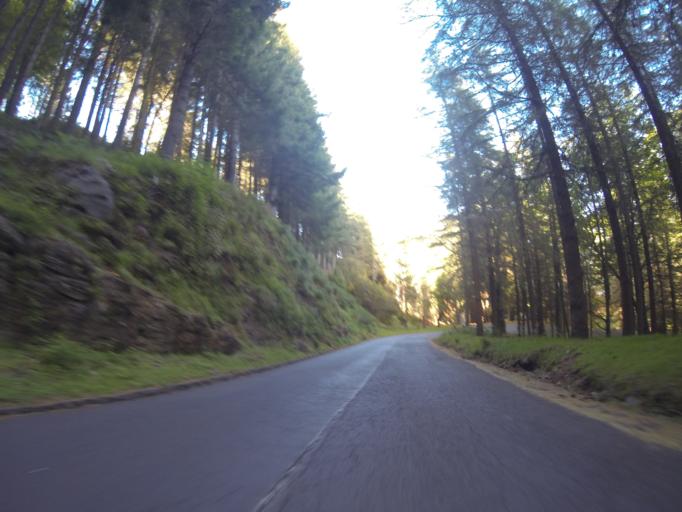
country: PT
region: Madeira
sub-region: Funchal
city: Nossa Senhora do Monte
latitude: 32.7024
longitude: -16.8813
